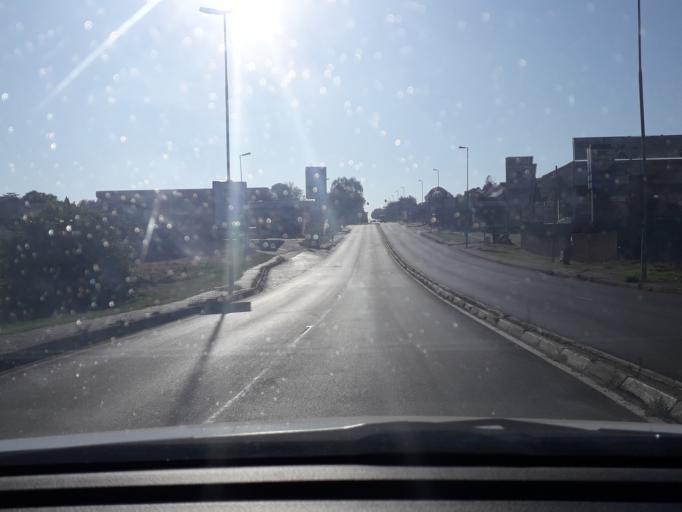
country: ZA
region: Gauteng
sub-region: City of Johannesburg Metropolitan Municipality
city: Johannesburg
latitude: -26.0984
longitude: 27.9912
